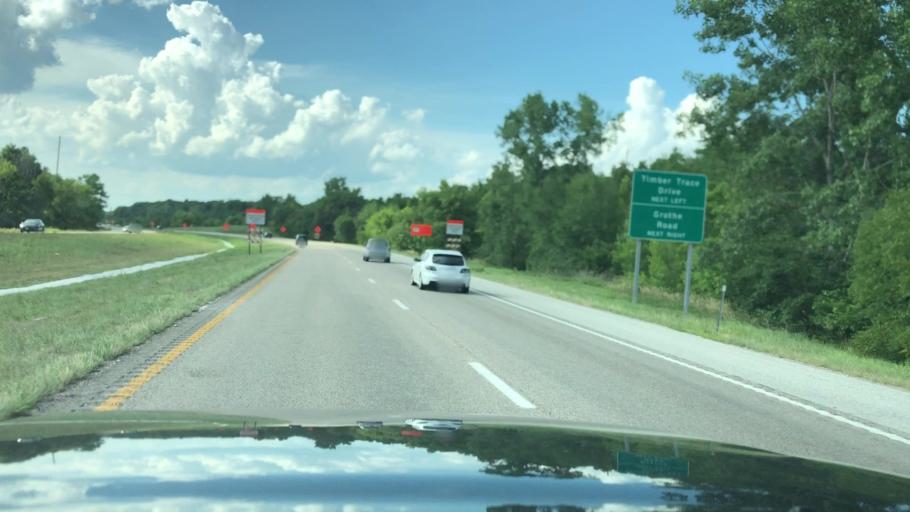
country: US
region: Missouri
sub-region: Saint Charles County
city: Wentzville
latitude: 38.8386
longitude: -90.8577
